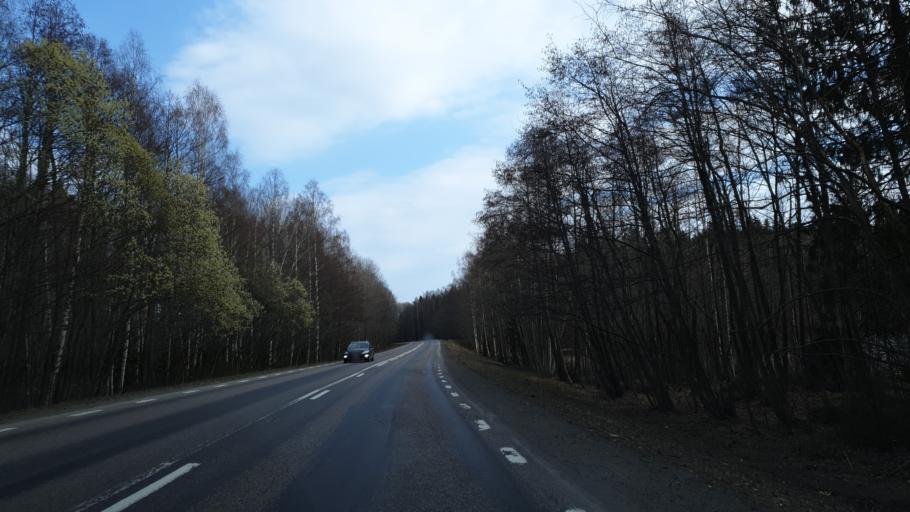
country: SE
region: Gaevleborg
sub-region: Hudiksvalls Kommun
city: Iggesund
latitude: 61.6479
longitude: 17.0461
